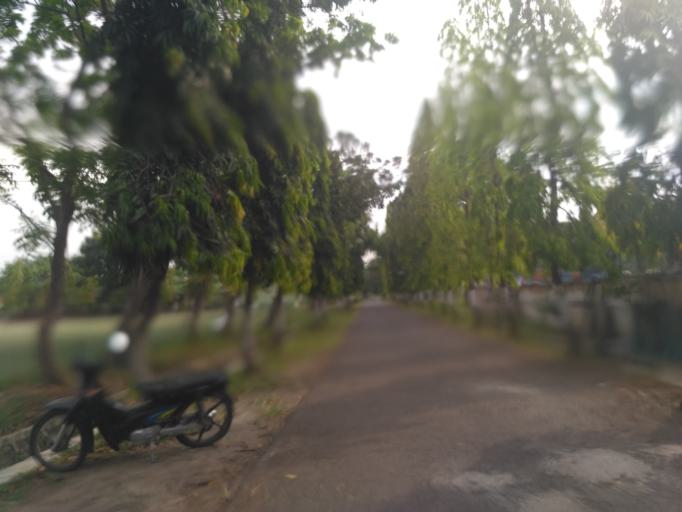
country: ID
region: Central Java
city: Semarang
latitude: -6.9888
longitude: 110.3759
